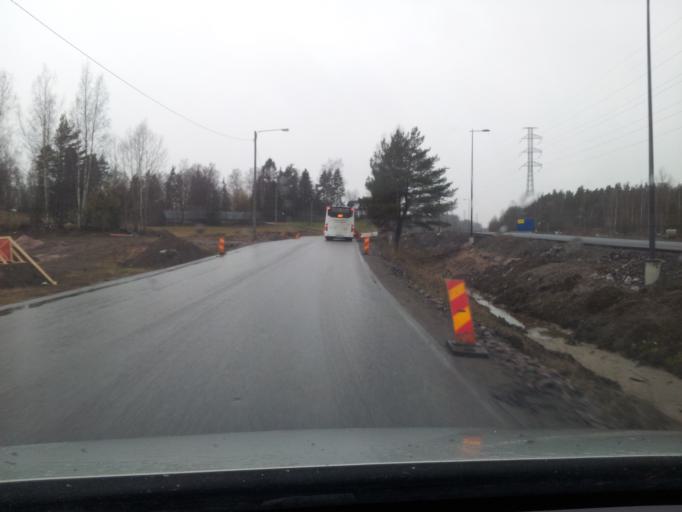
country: FI
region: Uusimaa
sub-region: Helsinki
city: Espoo
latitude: 60.1710
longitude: 24.6170
